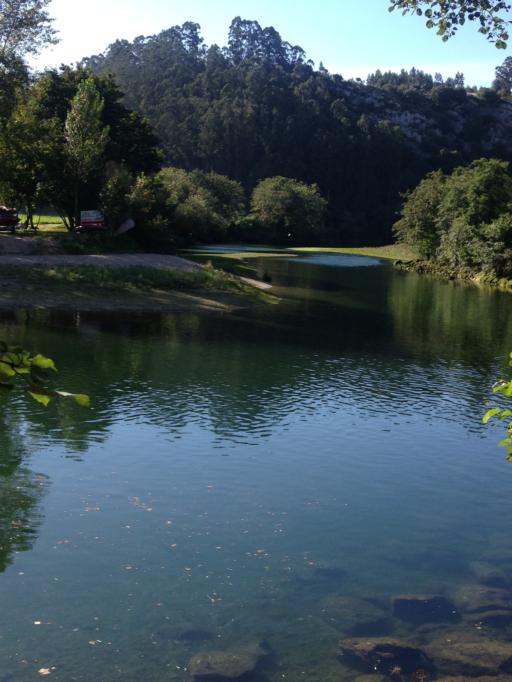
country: ES
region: Cantabria
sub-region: Provincia de Cantabria
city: San Vicente de la Barquera
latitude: 43.3664
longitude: -4.5202
